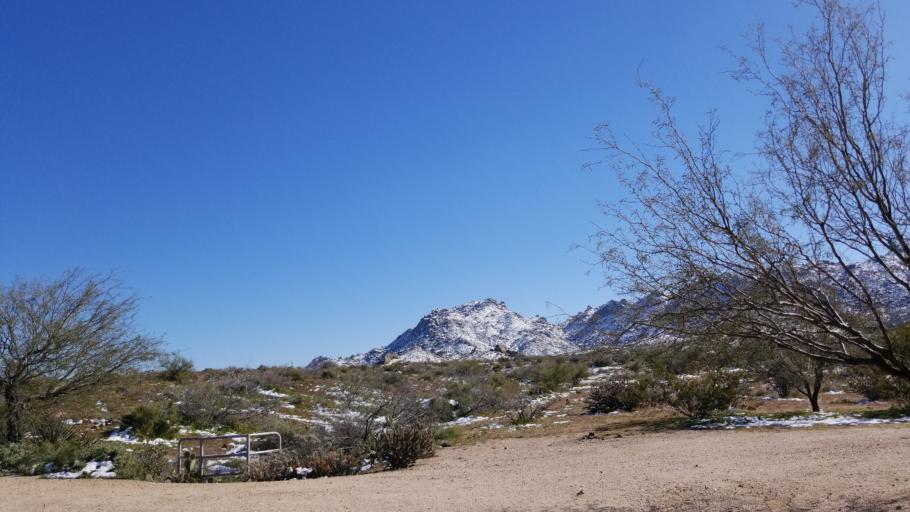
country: US
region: Arizona
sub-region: Maricopa County
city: Fountain Hills
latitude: 33.7045
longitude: -111.8165
